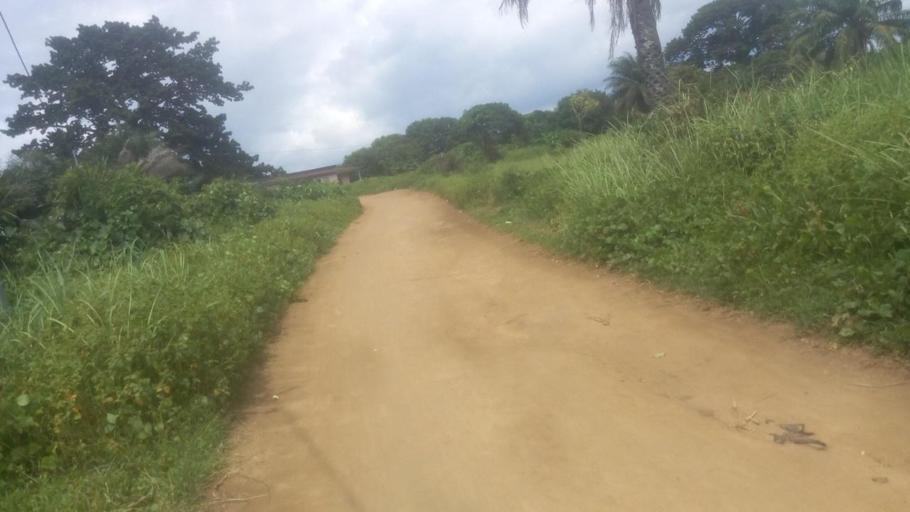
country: SL
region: Western Area
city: Freetown
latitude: 8.5255
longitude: -13.1462
